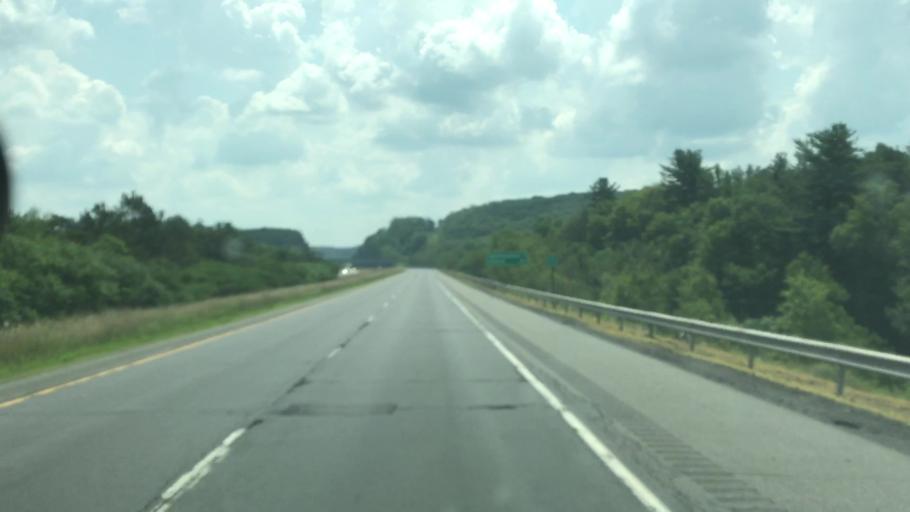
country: US
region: Pennsylvania
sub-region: Lackawanna County
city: Mount Cobb
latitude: 41.4003
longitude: -75.4890
